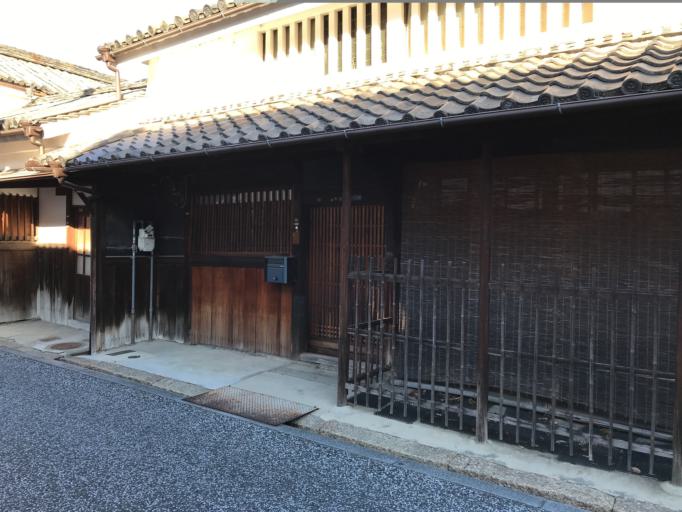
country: JP
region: Osaka
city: Tondabayashicho
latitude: 34.4994
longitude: 135.6019
